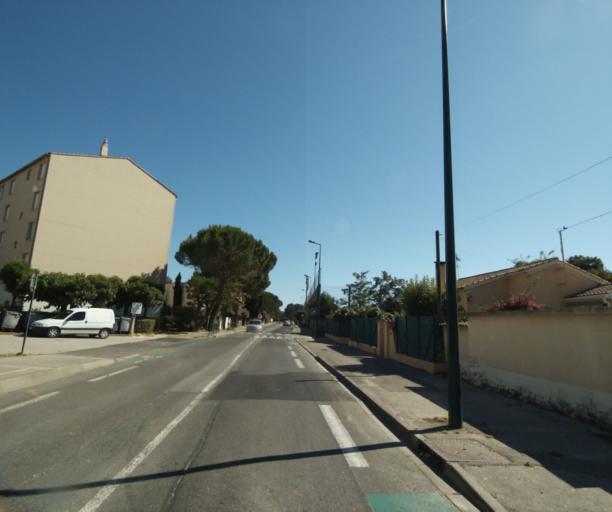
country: FR
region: Provence-Alpes-Cote d'Azur
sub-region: Departement du Var
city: La Garde
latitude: 43.1220
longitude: 6.0122
